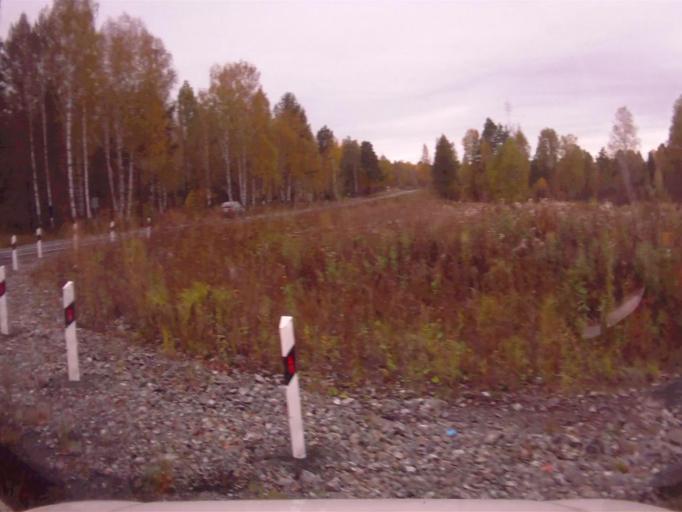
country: RU
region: Chelyabinsk
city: Nyazepetrovsk
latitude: 56.0442
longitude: 59.7685
